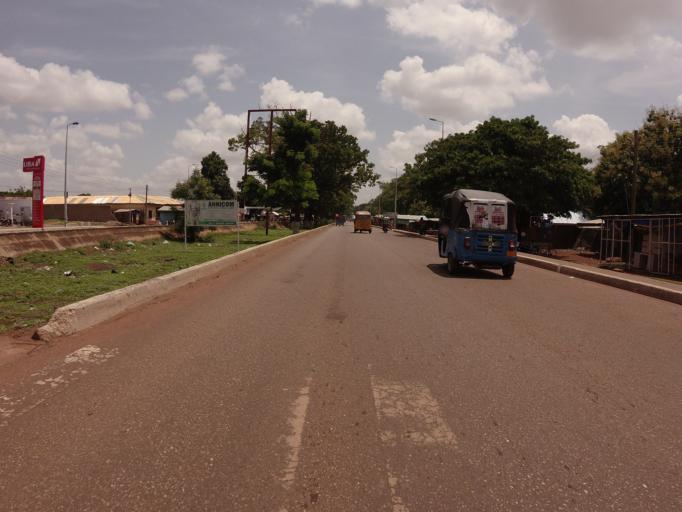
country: GH
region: Northern
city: Tamale
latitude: 9.4044
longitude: -0.8521
